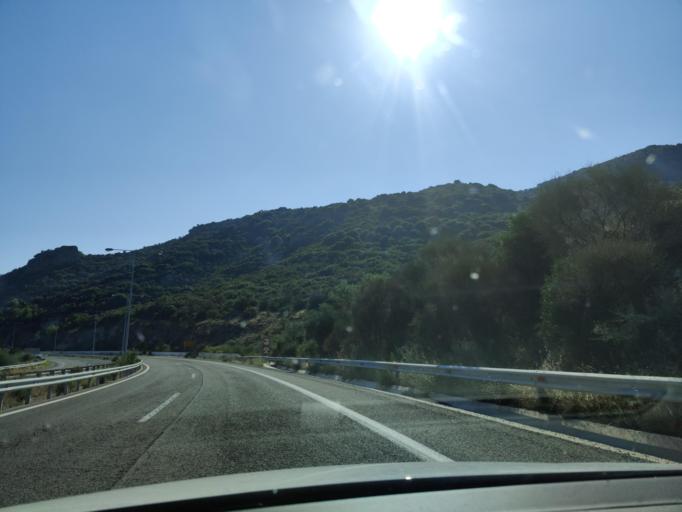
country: GR
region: East Macedonia and Thrace
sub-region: Nomos Kavalas
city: Palaio Tsifliki
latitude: 40.9095
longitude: 24.3448
